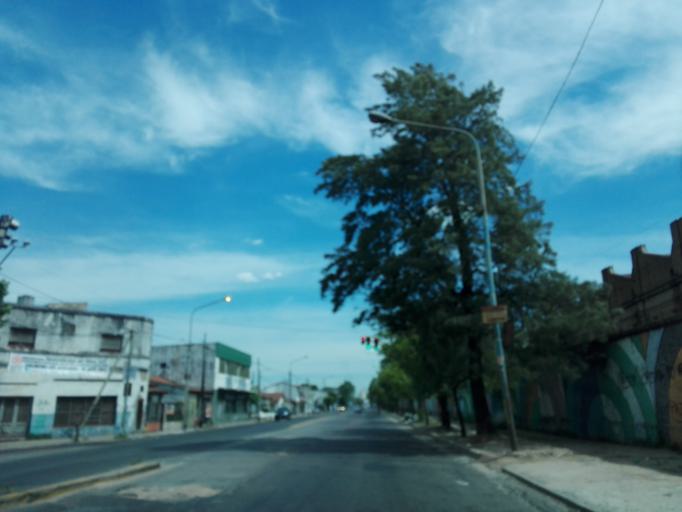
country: AR
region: Buenos Aires
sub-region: Partido de Lanus
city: Lanus
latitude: -34.7297
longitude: -58.3902
